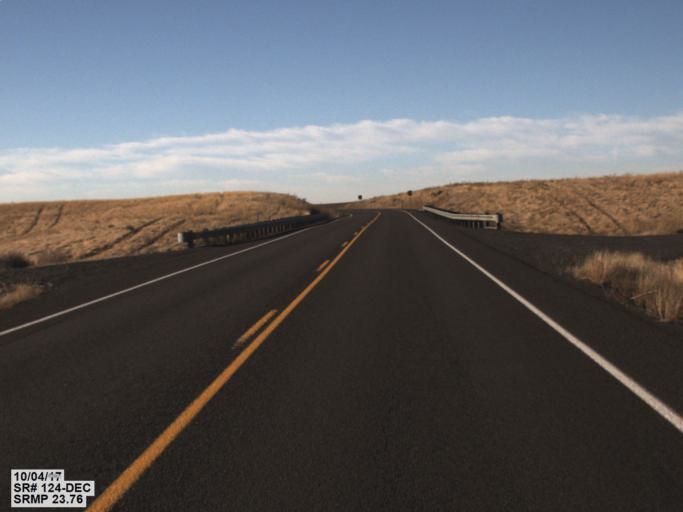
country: US
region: Washington
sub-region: Walla Walla County
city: Garrett
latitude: 46.2942
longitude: -118.5608
